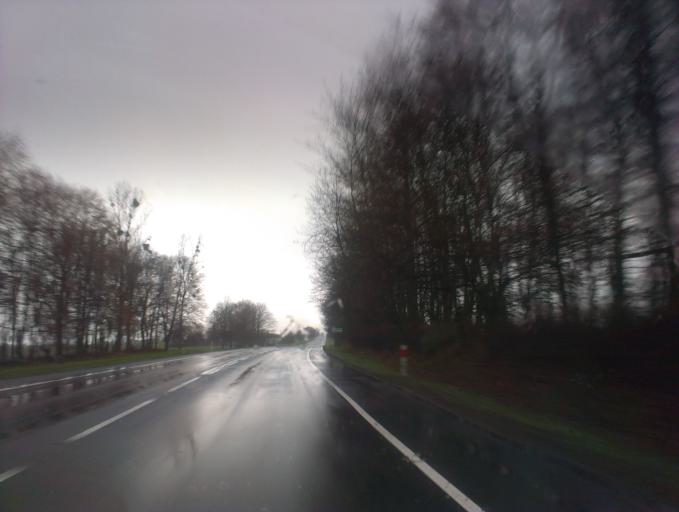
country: PL
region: Greater Poland Voivodeship
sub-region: Powiat pilski
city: Ujscie
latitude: 53.0314
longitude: 16.7849
